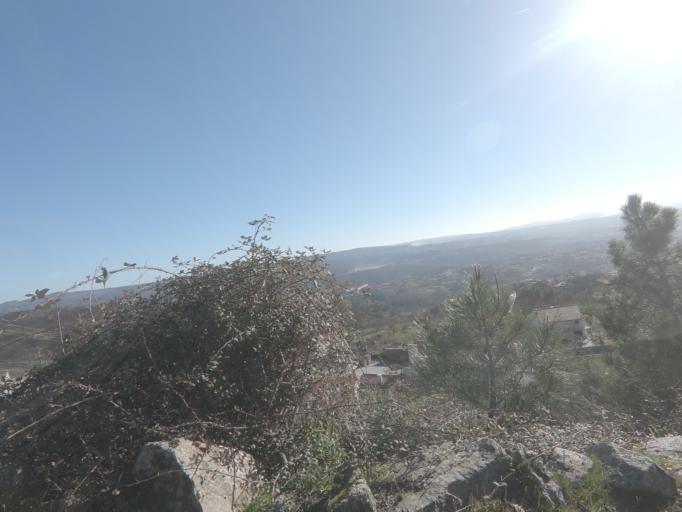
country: PT
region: Vila Real
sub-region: Vila Real
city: Vila Real
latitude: 41.3514
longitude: -7.7468
